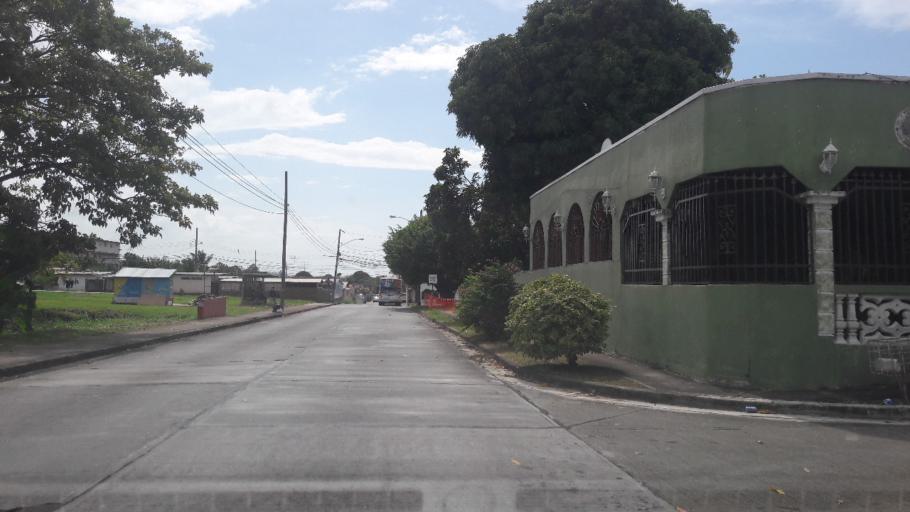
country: PA
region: Panama
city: Tocumen
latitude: 9.0532
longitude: -79.4184
